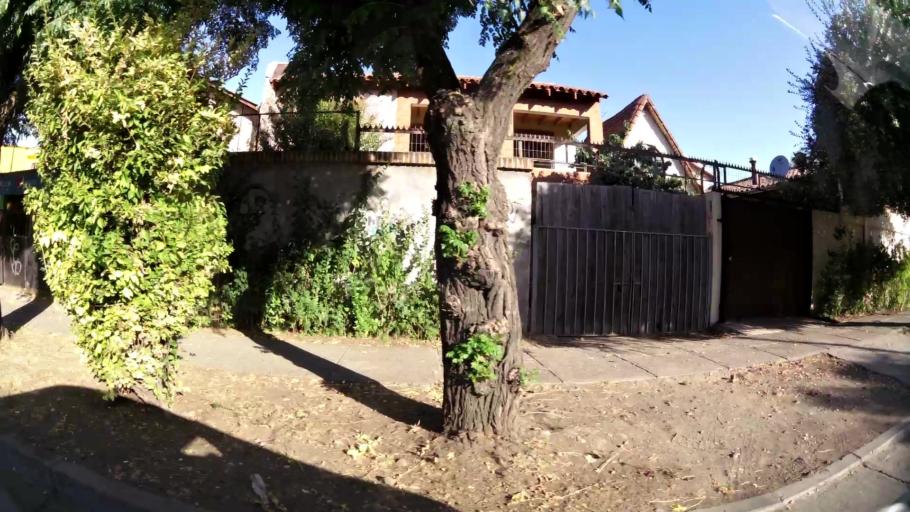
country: CL
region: Maule
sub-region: Provincia de Talca
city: Talca
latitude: -35.4375
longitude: -71.6867
